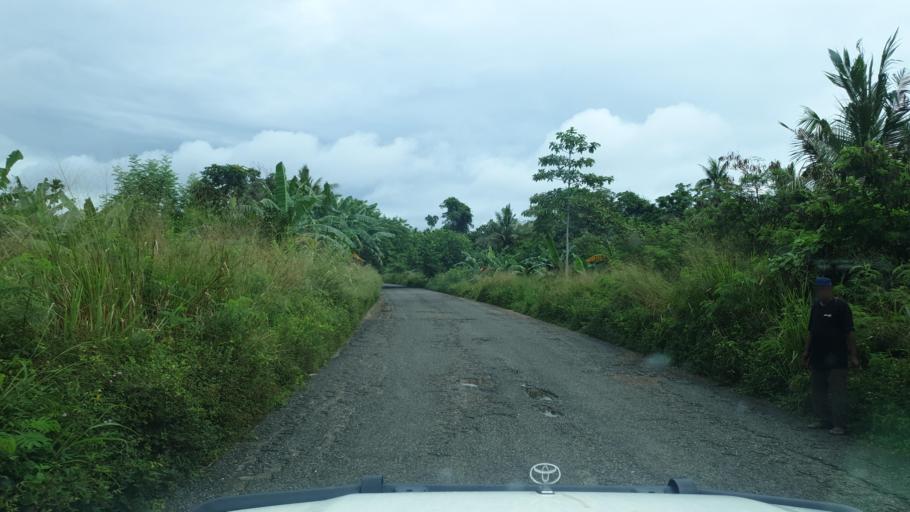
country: PG
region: Gulf
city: Kerema
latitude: -8.2431
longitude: 146.2885
